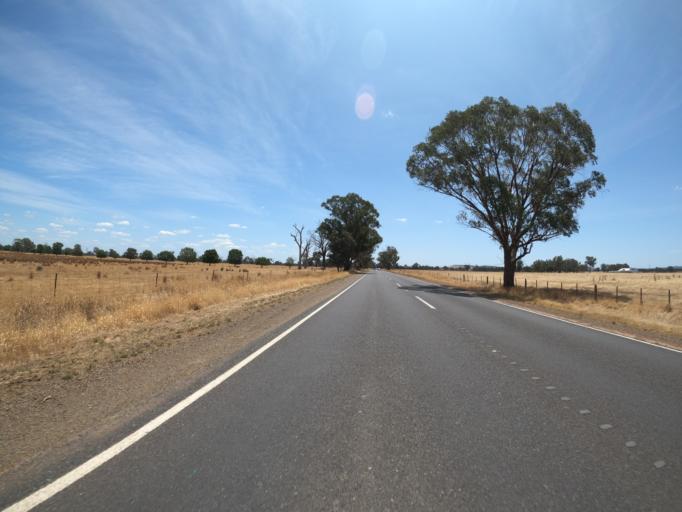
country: AU
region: Victoria
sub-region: Benalla
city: Benalla
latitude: -36.5147
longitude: 146.0311
